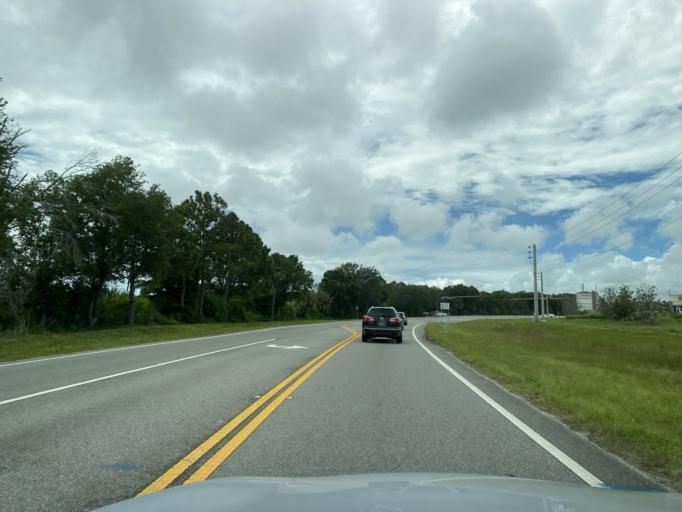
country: US
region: Florida
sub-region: Brevard County
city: West Melbourne
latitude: 28.0385
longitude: -80.6512
